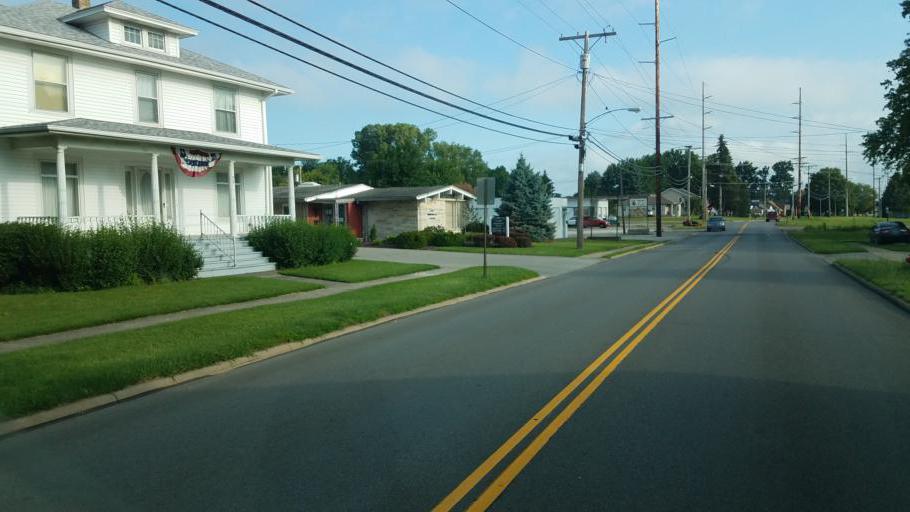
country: US
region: Ohio
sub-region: Richland County
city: Shelby
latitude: 40.8887
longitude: -82.6624
